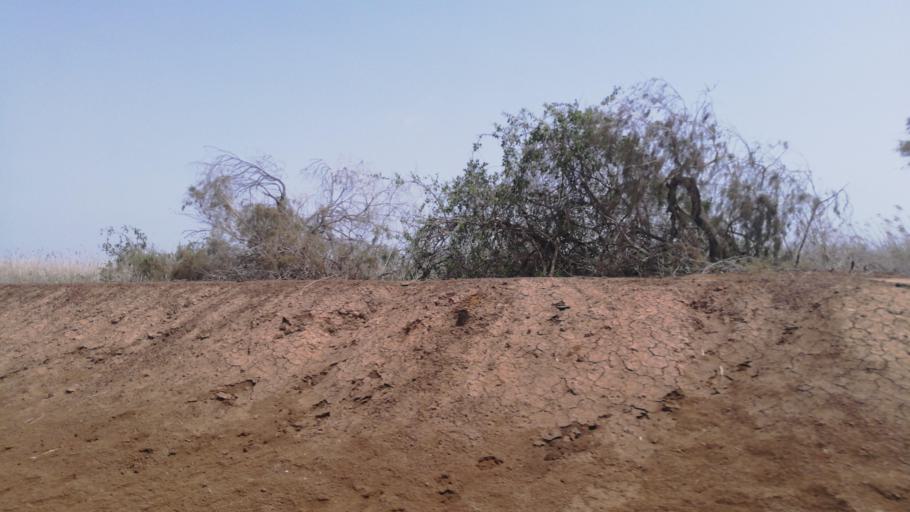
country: SN
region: Saint-Louis
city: Saint-Louis
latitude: 16.4006
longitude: -16.2899
